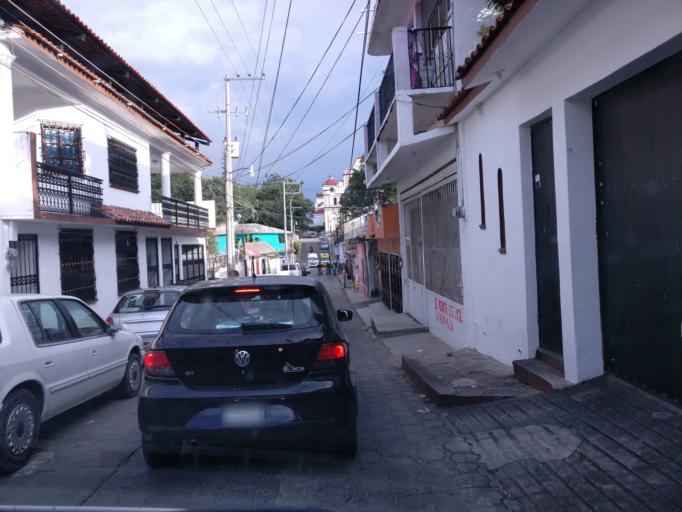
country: MX
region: Chiapas
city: Chiapa de Corzo
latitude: 16.7078
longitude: -93.0193
